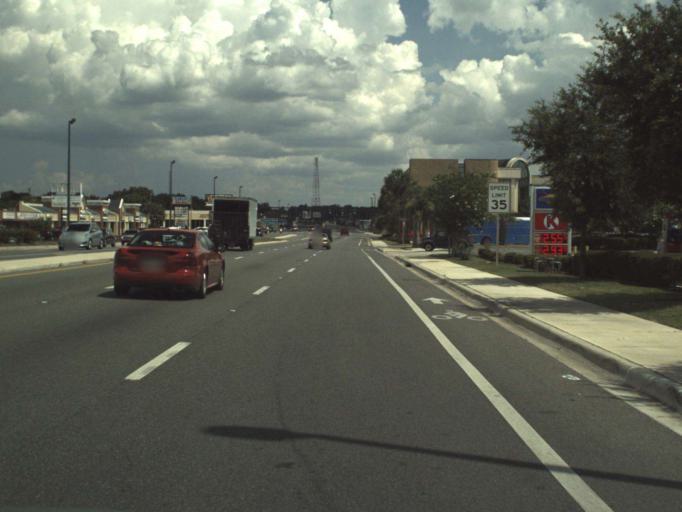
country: US
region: Florida
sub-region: Lake County
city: Leesburg
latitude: 28.8245
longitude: -81.8855
